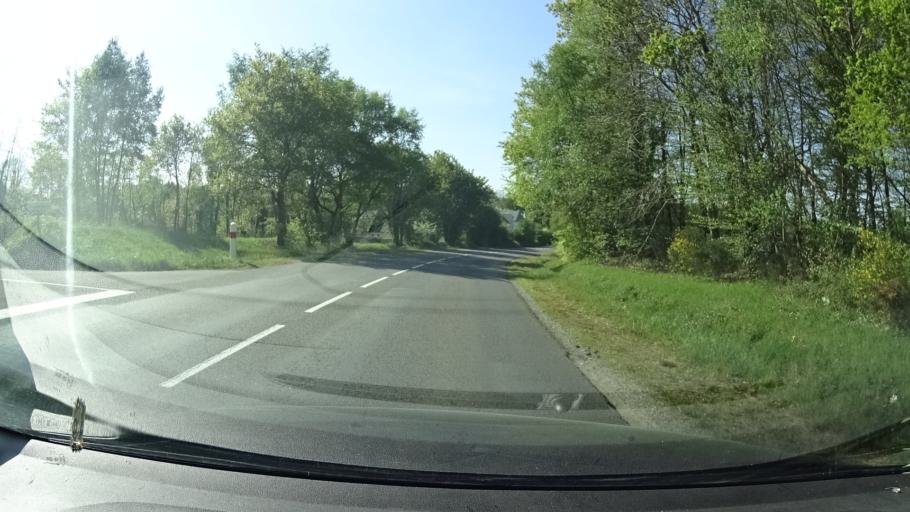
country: FR
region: Brittany
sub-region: Departement du Finistere
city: Mellac
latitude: 47.8889
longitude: -3.5750
